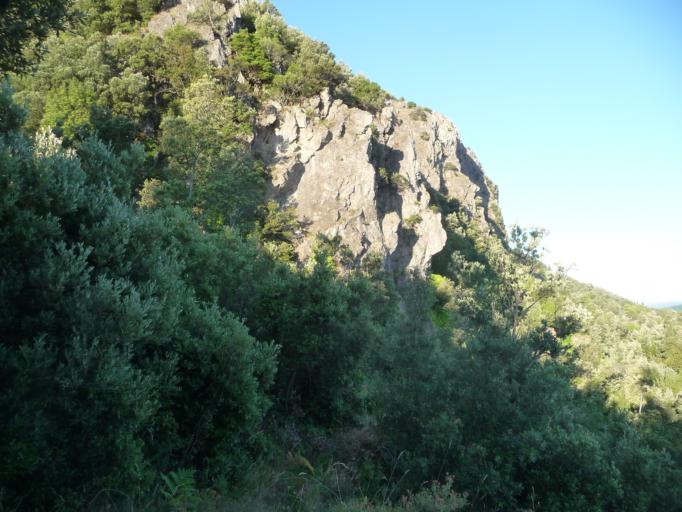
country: IT
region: Calabria
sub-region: Provincia di Reggio Calabria
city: Pazzano
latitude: 38.4629
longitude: 16.4286
